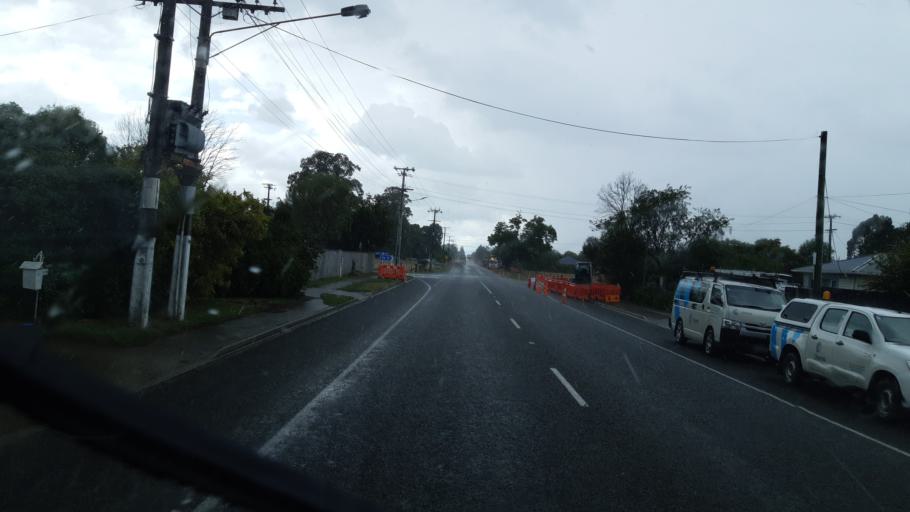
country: NZ
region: Tasman
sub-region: Tasman District
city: Wakefield
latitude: -41.3995
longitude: 173.0591
